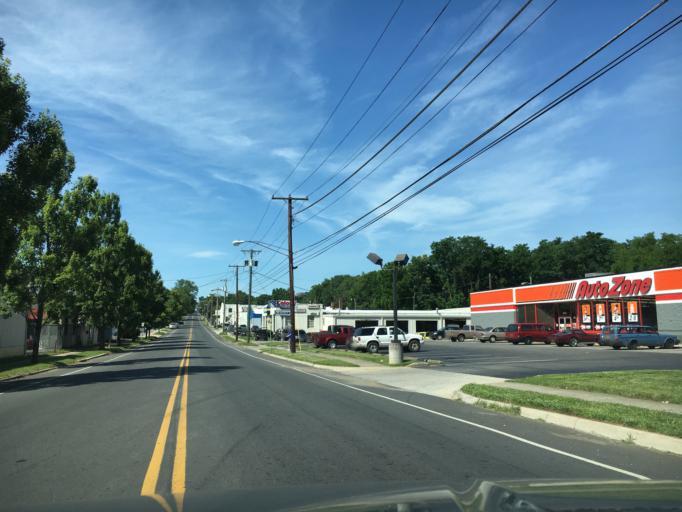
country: US
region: Virginia
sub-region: City of Lynchburg
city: West Lynchburg
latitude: 37.4000
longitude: -79.1621
